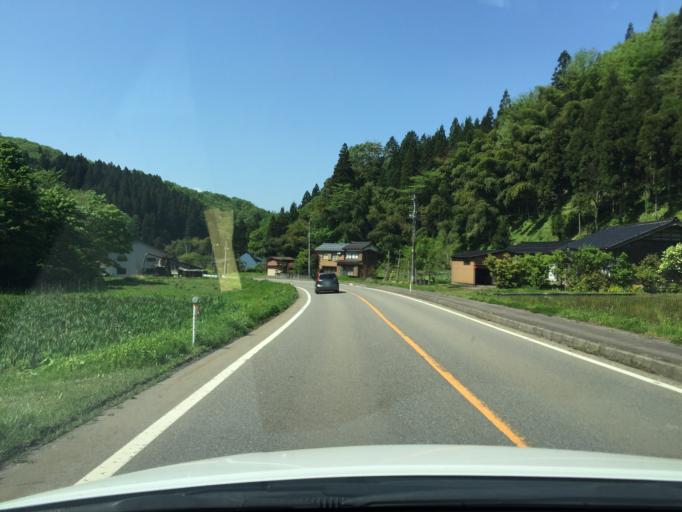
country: JP
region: Niigata
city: Kamo
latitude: 37.6377
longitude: 139.1105
